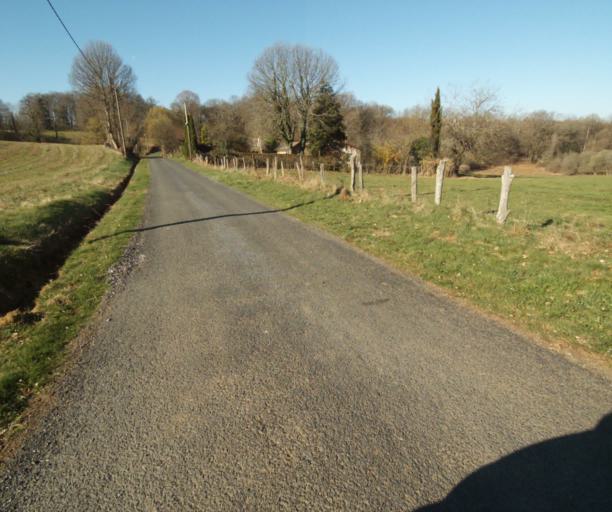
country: FR
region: Limousin
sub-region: Departement de la Correze
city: Saint-Clement
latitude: 45.3796
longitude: 1.6432
